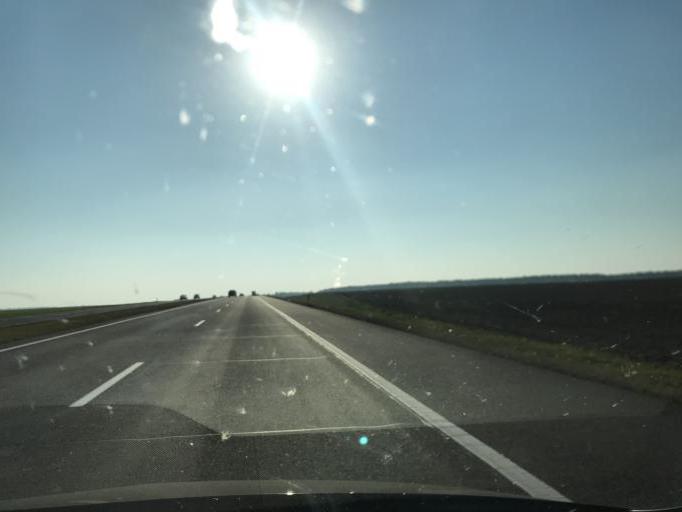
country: BY
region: Grodnenskaya
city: Mir
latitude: 53.4278
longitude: 26.5818
